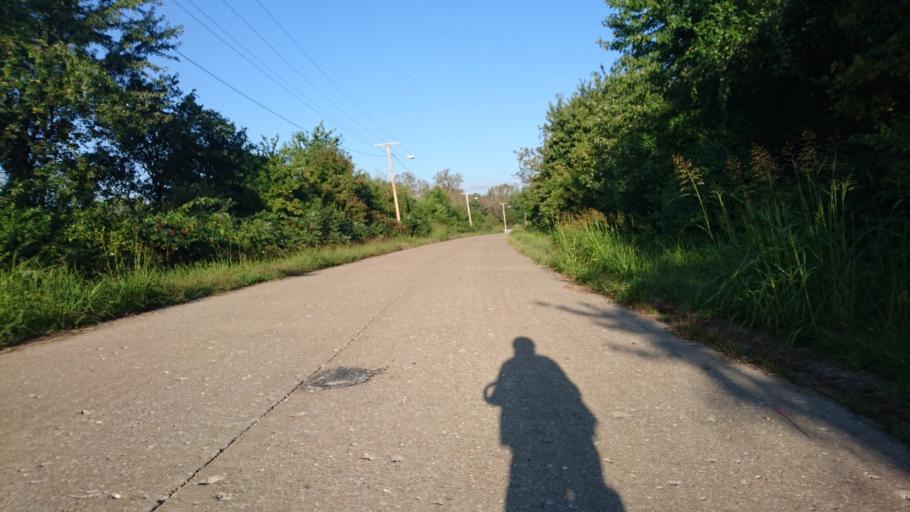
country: US
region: Missouri
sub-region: Saint Louis County
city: Glasgow Village
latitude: 38.7565
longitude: -90.1622
